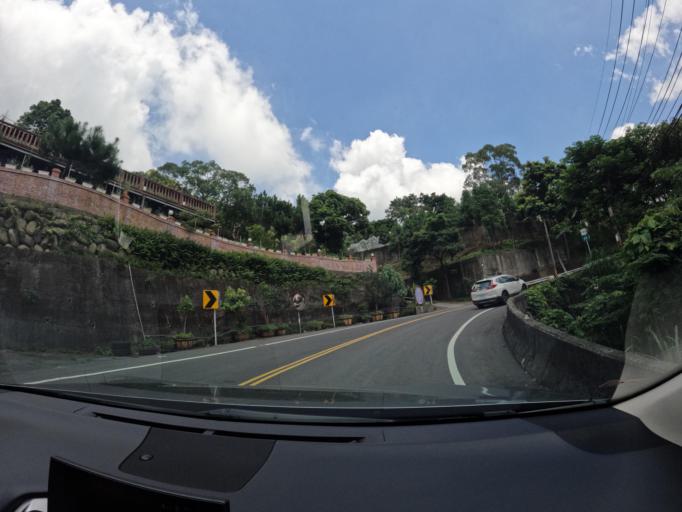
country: TW
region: Taiwan
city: Fengyuan
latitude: 24.3876
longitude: 120.8187
